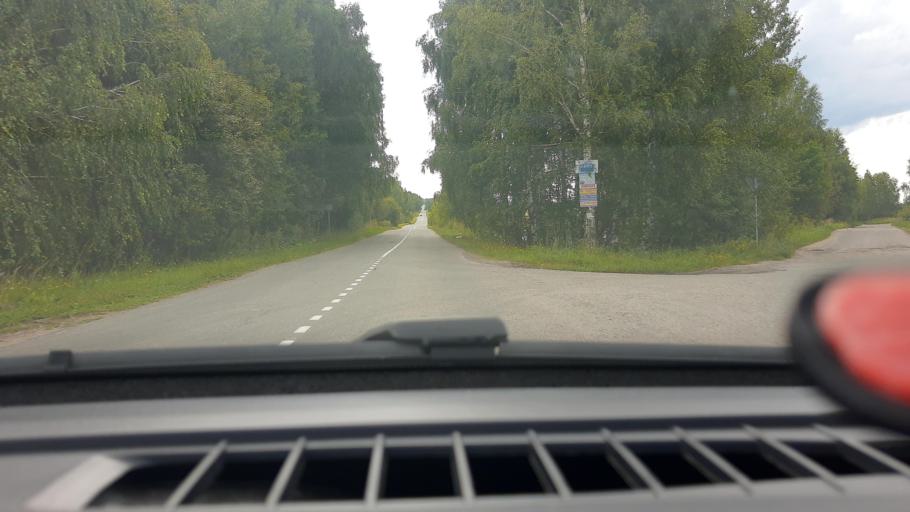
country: RU
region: Nizjnij Novgorod
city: Burevestnik
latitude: 56.0523
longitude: 43.6943
